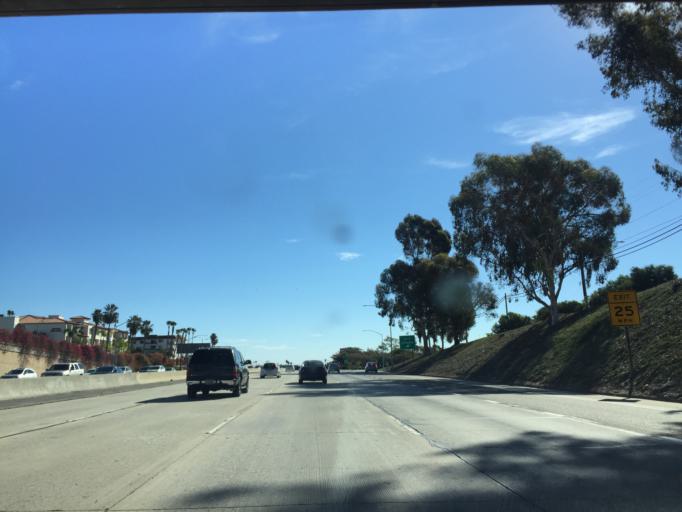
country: US
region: California
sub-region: Orange County
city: San Clemente
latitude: 33.4114
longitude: -117.6015
